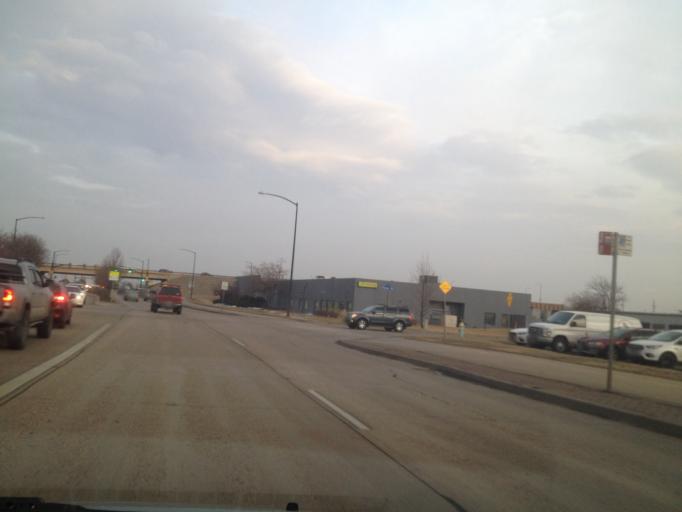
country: US
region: Colorado
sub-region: Boulder County
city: Boulder
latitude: 40.0229
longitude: -105.2479
